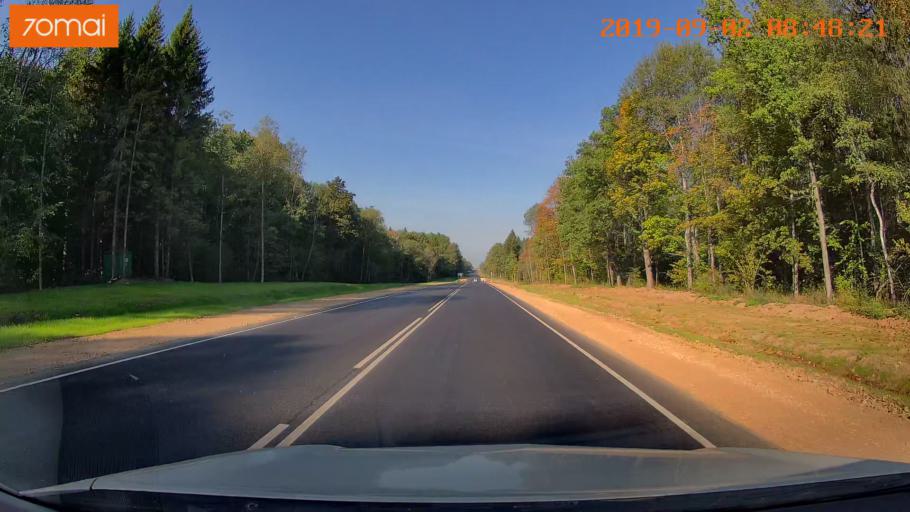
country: RU
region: Kaluga
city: Medyn'
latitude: 54.9671
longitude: 35.9343
